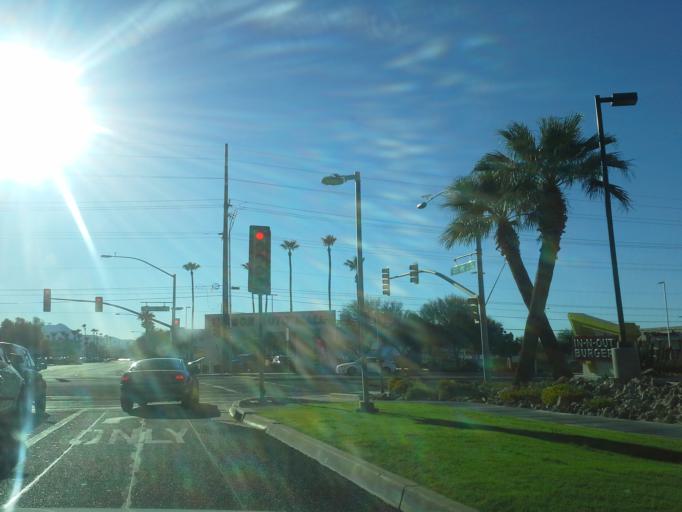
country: US
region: Arizona
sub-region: Pima County
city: Flowing Wells
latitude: 32.2904
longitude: -110.9771
